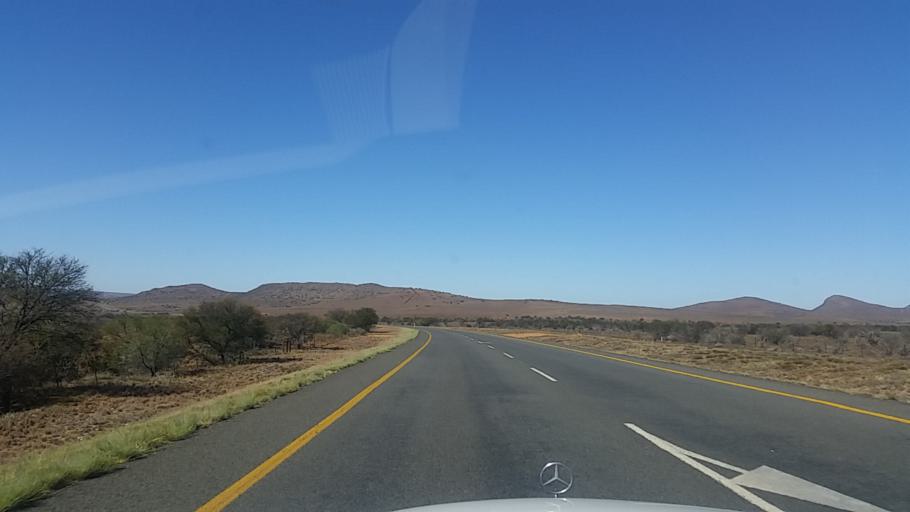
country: ZA
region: Eastern Cape
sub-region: Cacadu District Municipality
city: Graaff-Reinet
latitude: -32.0744
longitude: 24.6037
